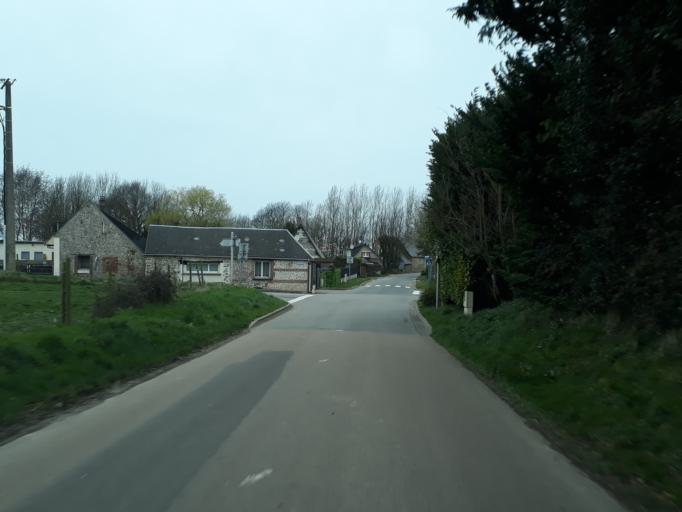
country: FR
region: Haute-Normandie
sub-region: Departement de la Seine-Maritime
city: Les Loges
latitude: 49.7216
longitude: 0.2807
